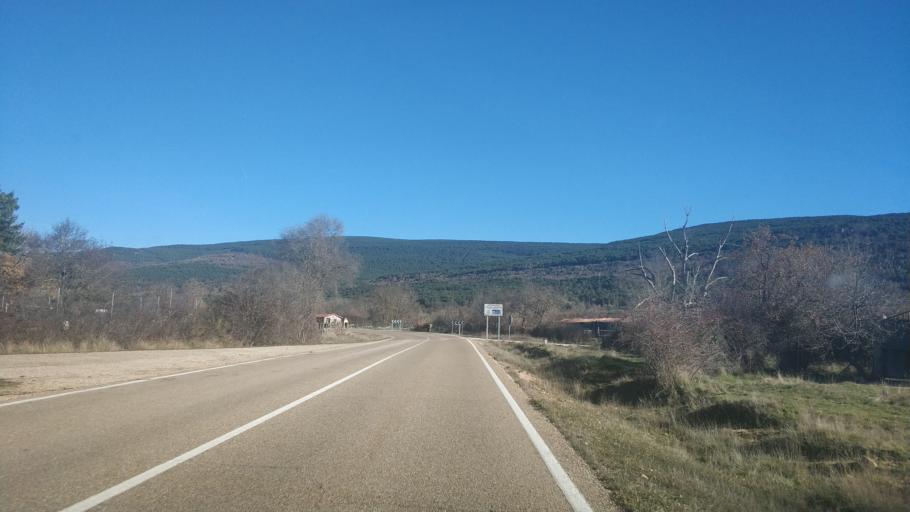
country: ES
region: Castille and Leon
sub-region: Provincia de Soria
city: Vinuesa
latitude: 41.9142
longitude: -2.7550
